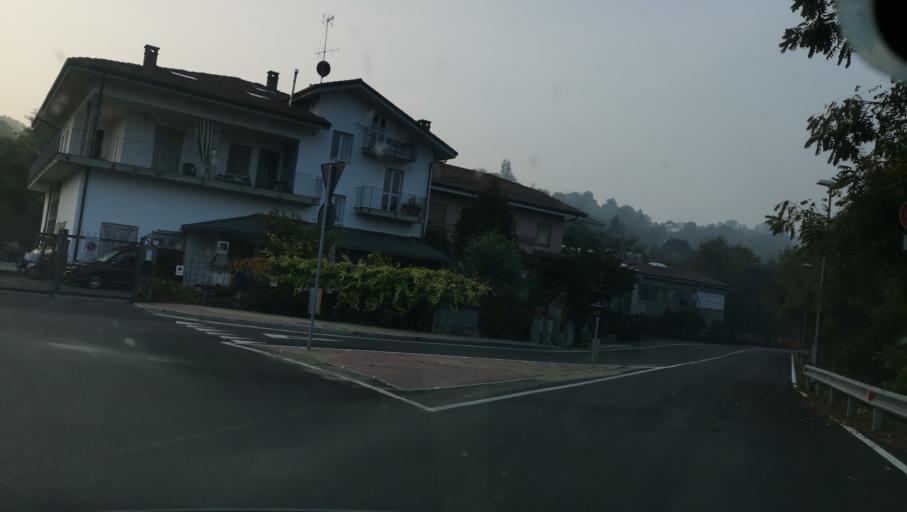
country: IT
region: Piedmont
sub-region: Provincia di Torino
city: Castiglione Torinese
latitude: 45.1228
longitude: 7.8123
